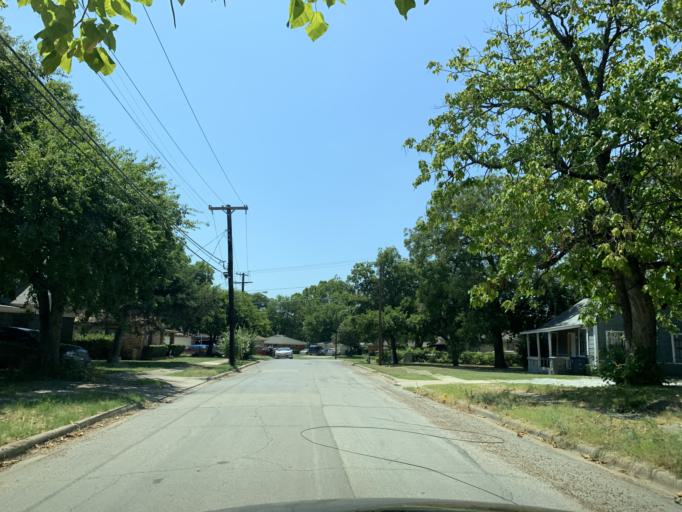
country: US
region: Texas
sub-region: Dallas County
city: Dallas
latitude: 32.6906
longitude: -96.8053
